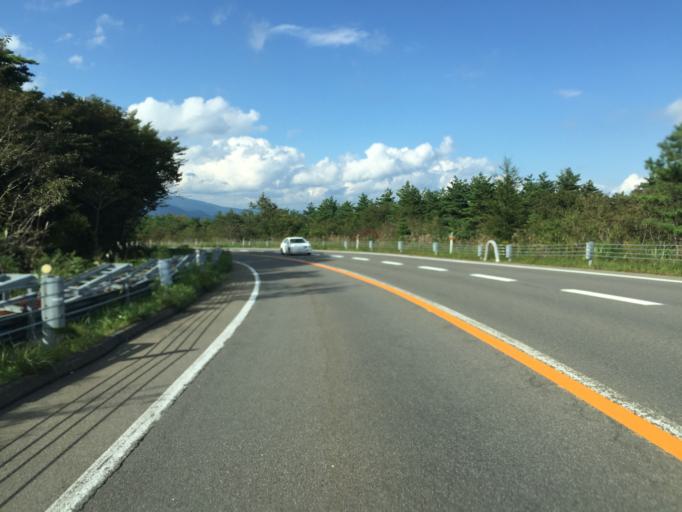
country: JP
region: Fukushima
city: Nihommatsu
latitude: 37.6515
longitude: 140.3307
